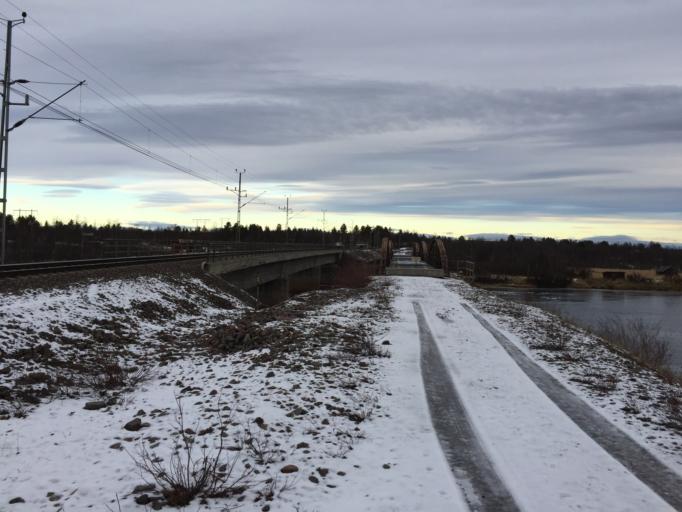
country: SE
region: Norrbotten
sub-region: Kiruna Kommun
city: Kiruna
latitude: 67.5402
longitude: 20.1000
